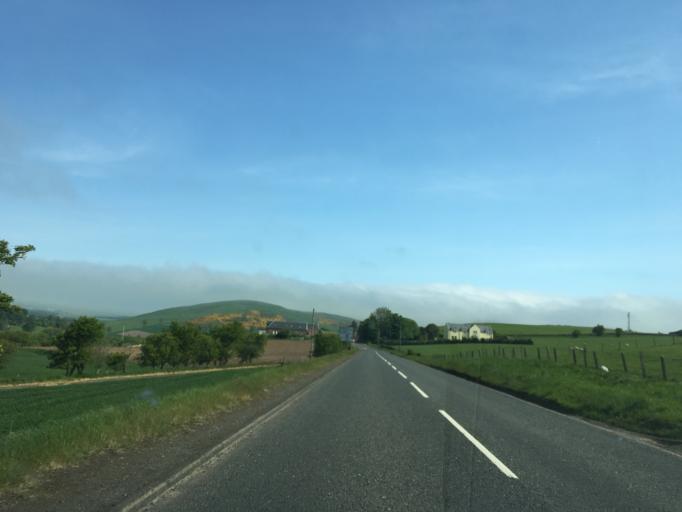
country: GB
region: Scotland
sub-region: The Scottish Borders
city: West Linton
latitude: 55.6823
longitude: -3.4003
